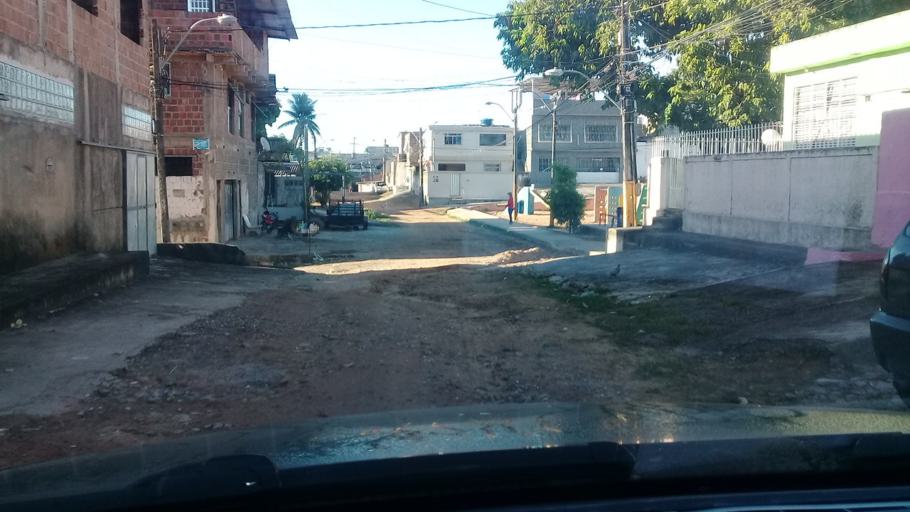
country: BR
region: Pernambuco
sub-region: Jaboatao Dos Guararapes
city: Jaboatao dos Guararapes
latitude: -8.1186
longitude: -34.9535
